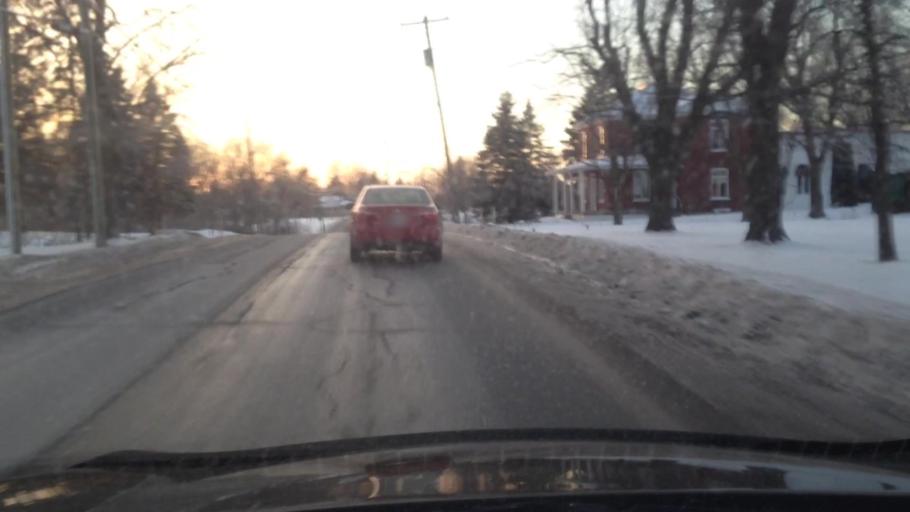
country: CA
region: Quebec
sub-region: Lanaudiere
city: Saint-Lin-Laurentides
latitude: 45.8520
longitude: -73.7615
